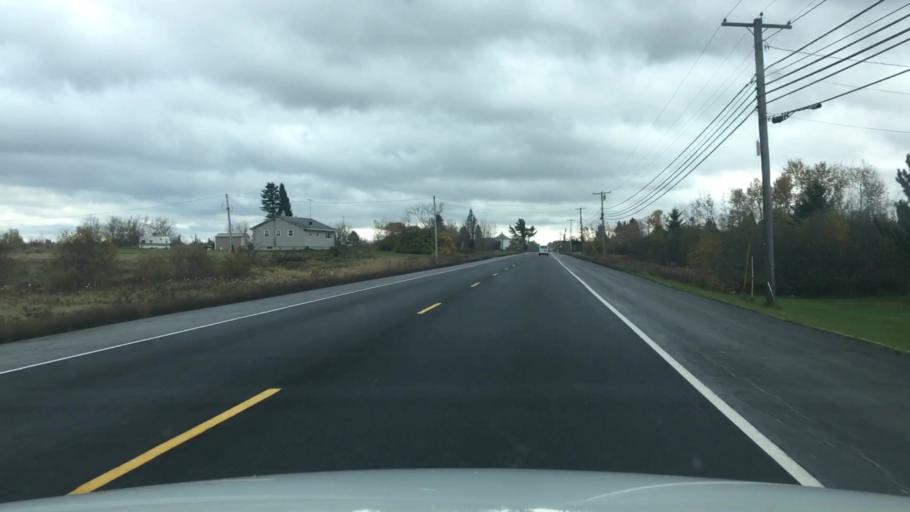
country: US
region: Maine
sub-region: Aroostook County
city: Houlton
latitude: 46.2528
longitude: -67.8409
